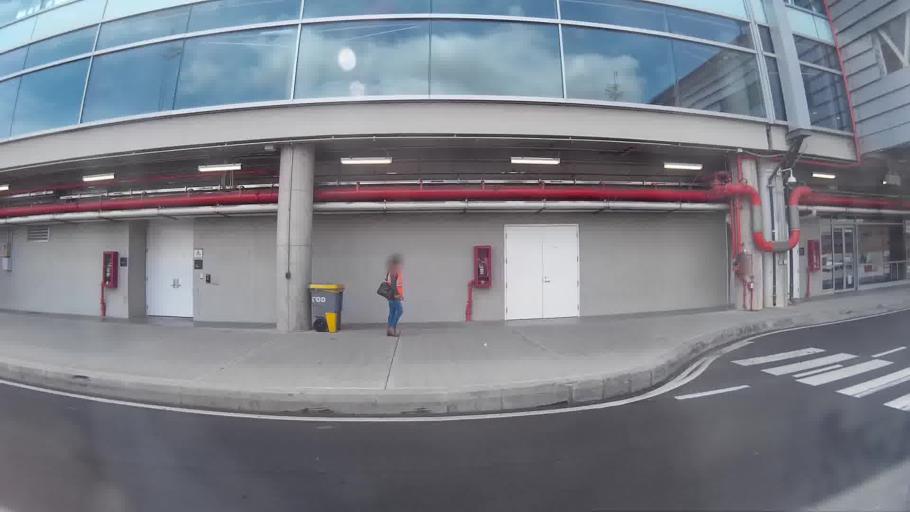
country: CO
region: Cundinamarca
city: Funza
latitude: 4.7004
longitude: -74.1433
